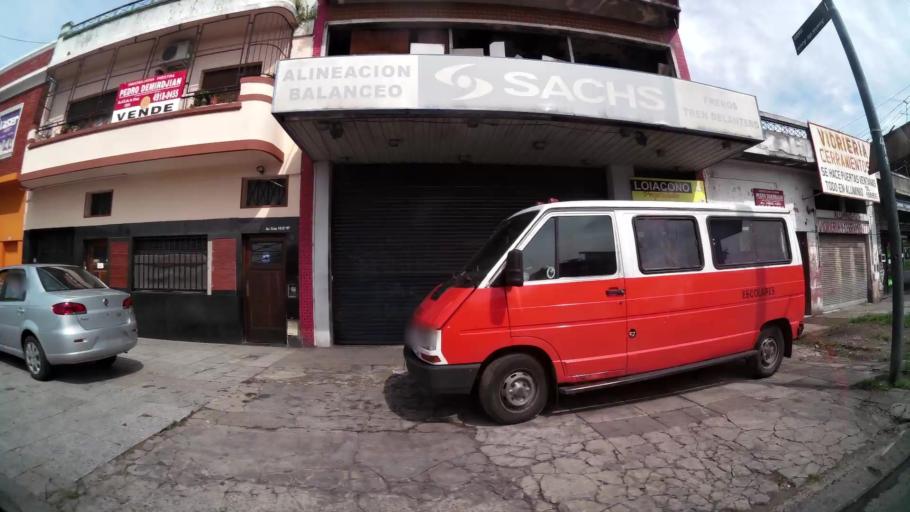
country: AR
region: Buenos Aires F.D.
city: Villa Lugano
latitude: -34.6482
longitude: -58.4286
